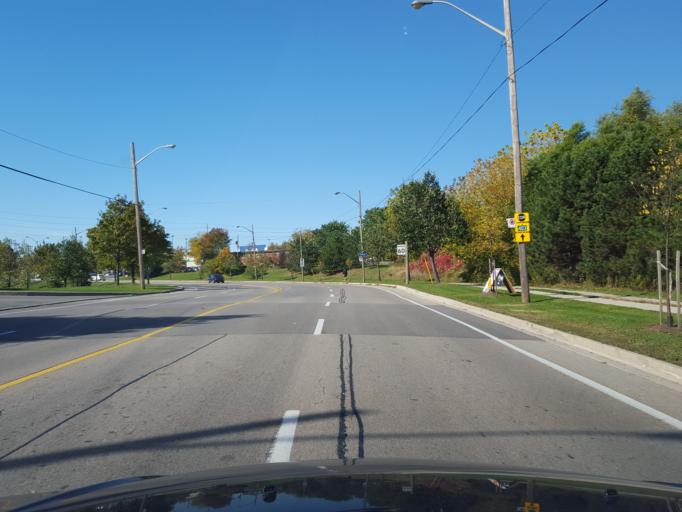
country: CA
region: Ontario
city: Burlington
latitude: 43.3451
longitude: -79.8233
